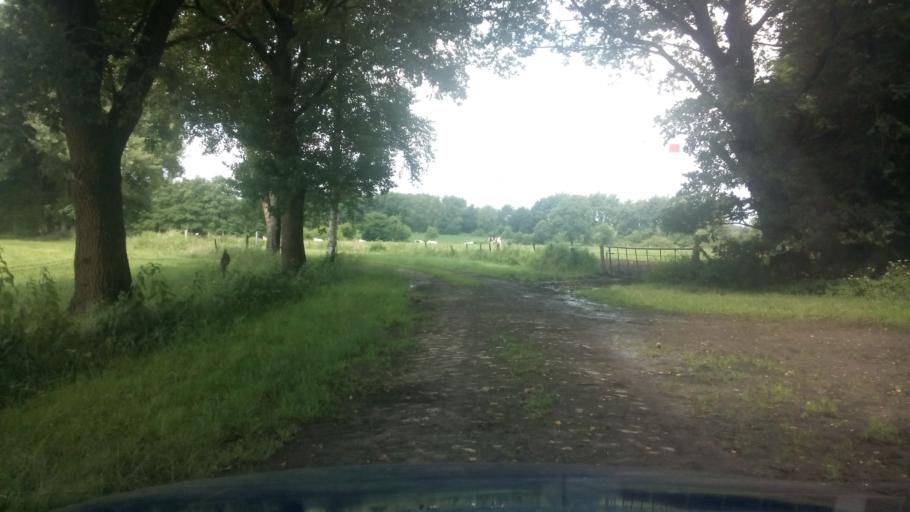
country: DE
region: Lower Saxony
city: Osterholz-Scharmbeck
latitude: 53.2366
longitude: 8.7461
